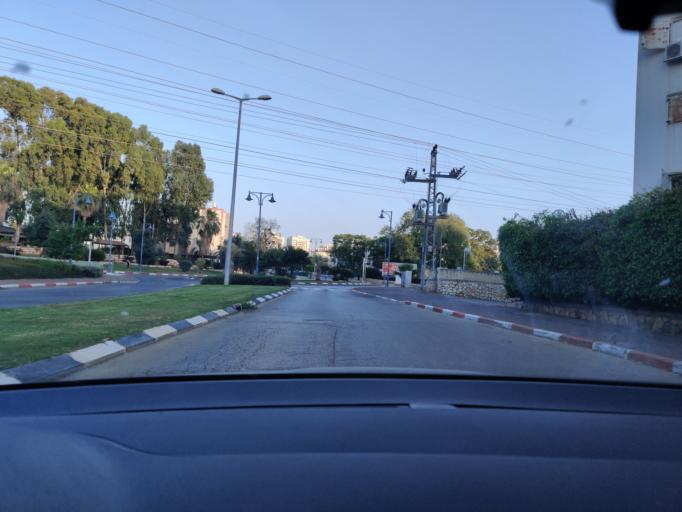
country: IL
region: Haifa
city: Hadera
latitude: 32.4739
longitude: 34.9519
